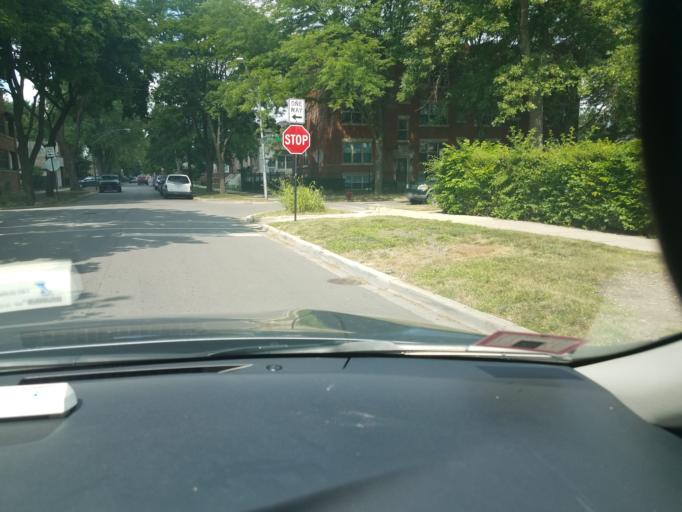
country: US
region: Illinois
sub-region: Cook County
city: Lincolnwood
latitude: 41.9645
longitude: -87.7396
